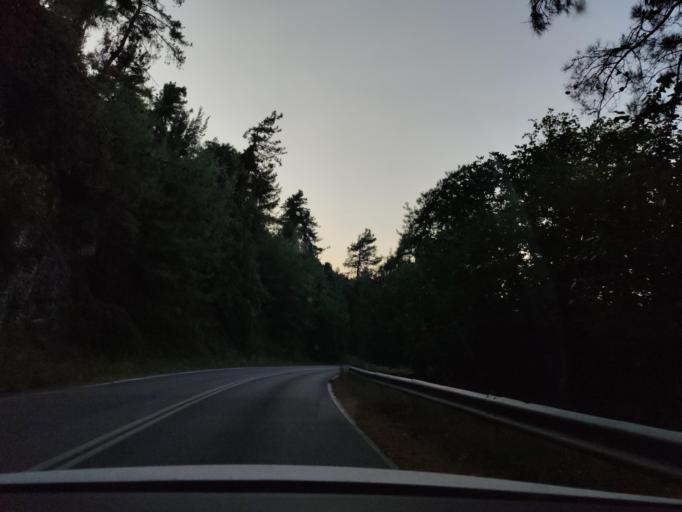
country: GR
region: East Macedonia and Thrace
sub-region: Nomos Kavalas
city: Potamia
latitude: 40.7058
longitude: 24.7674
